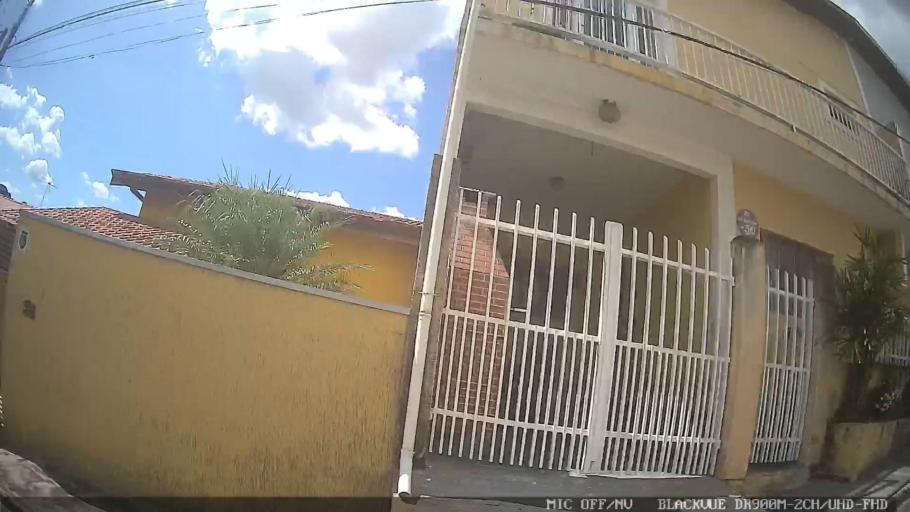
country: BR
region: Sao Paulo
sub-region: Atibaia
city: Atibaia
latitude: -23.1454
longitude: -46.5567
